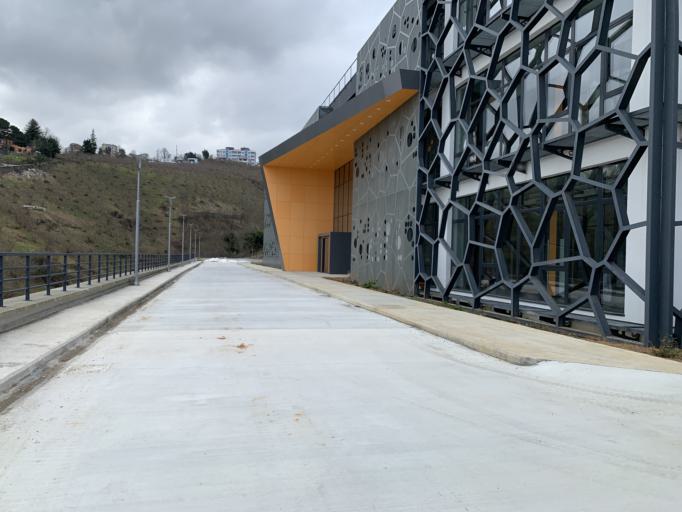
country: TR
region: Trabzon
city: Trabzon
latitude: 40.9905
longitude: 39.7755
